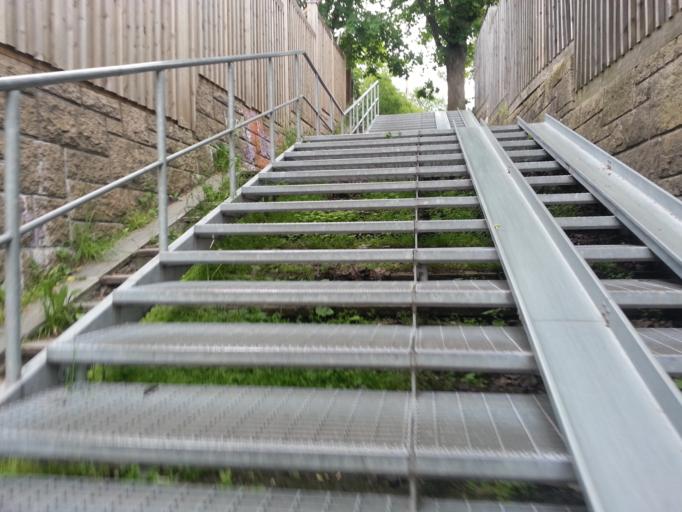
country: NO
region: Oslo
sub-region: Oslo
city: Sjolyststranda
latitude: 59.9345
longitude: 10.6981
